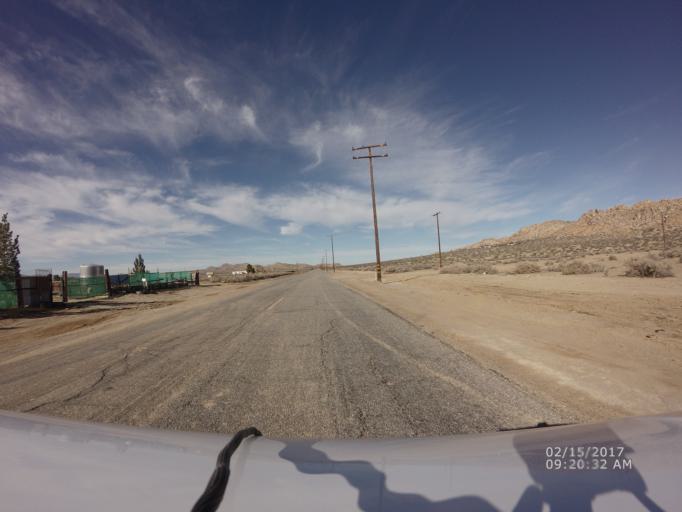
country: US
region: California
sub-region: Los Angeles County
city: Lake Los Angeles
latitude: 34.6458
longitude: -117.8425
